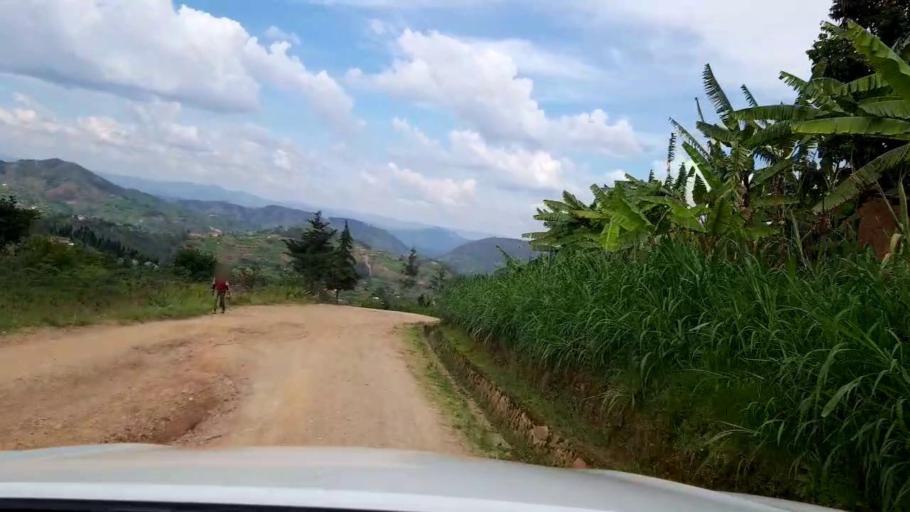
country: RW
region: Southern Province
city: Gitarama
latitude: -1.9804
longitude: 29.7103
